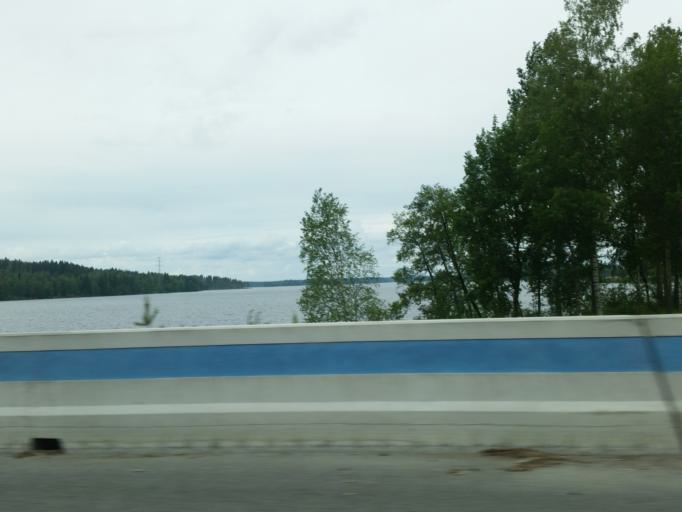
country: FI
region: Northern Savo
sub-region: Kuopio
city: Kuopio
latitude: 62.9425
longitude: 27.6678
